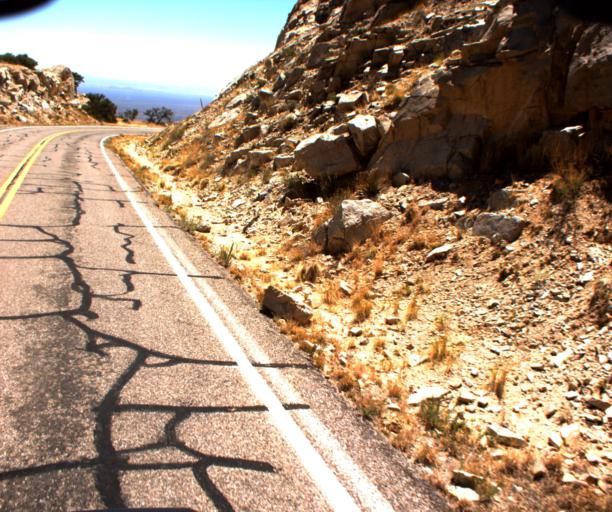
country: US
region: Arizona
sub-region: Pima County
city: Sells
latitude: 31.9511
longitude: -111.6238
